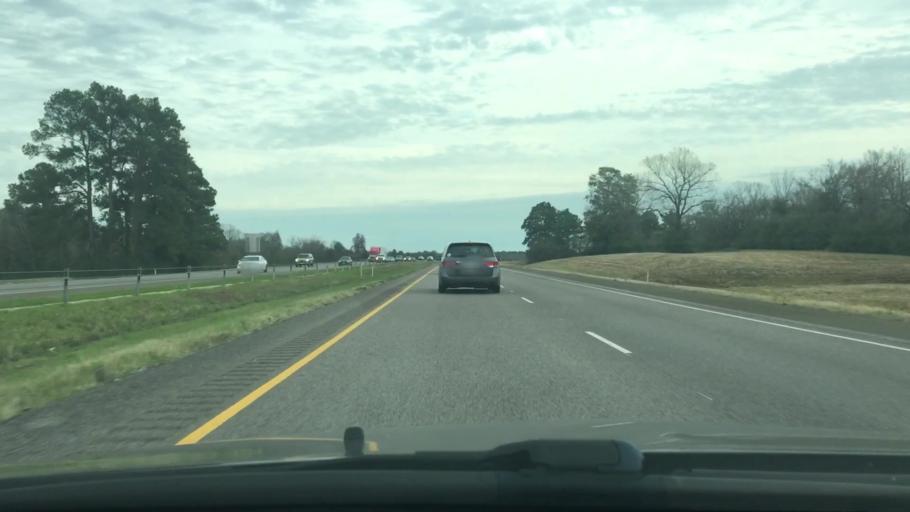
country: US
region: Texas
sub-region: Madison County
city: Madisonville
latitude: 30.9115
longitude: -95.7935
